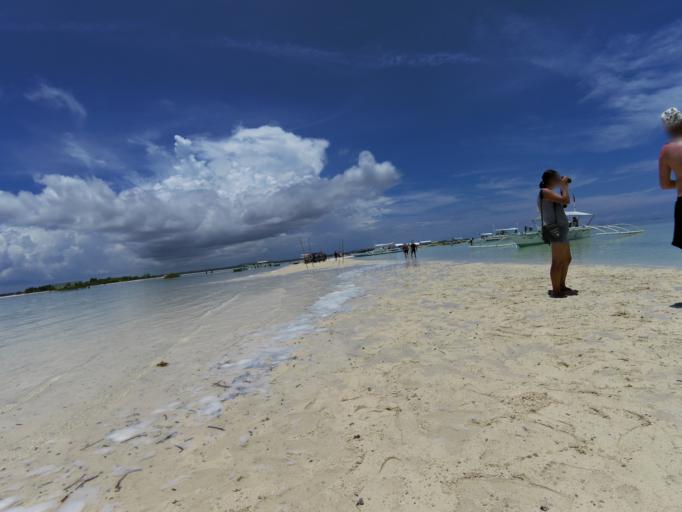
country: PH
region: Central Visayas
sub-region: Province of Bohol
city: Doljo
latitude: 9.5561
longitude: 123.7170
